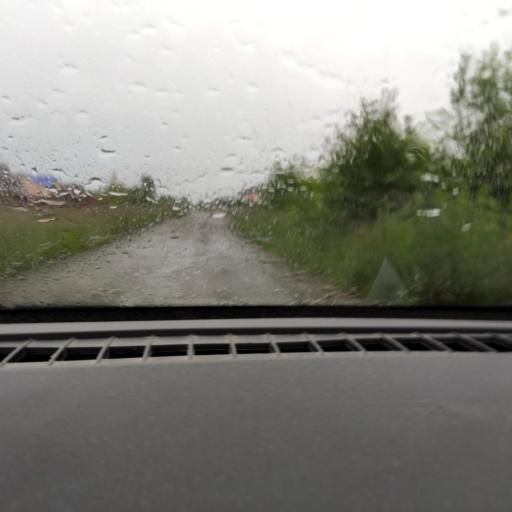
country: RU
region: Perm
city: Perm
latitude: 58.0417
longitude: 56.3732
